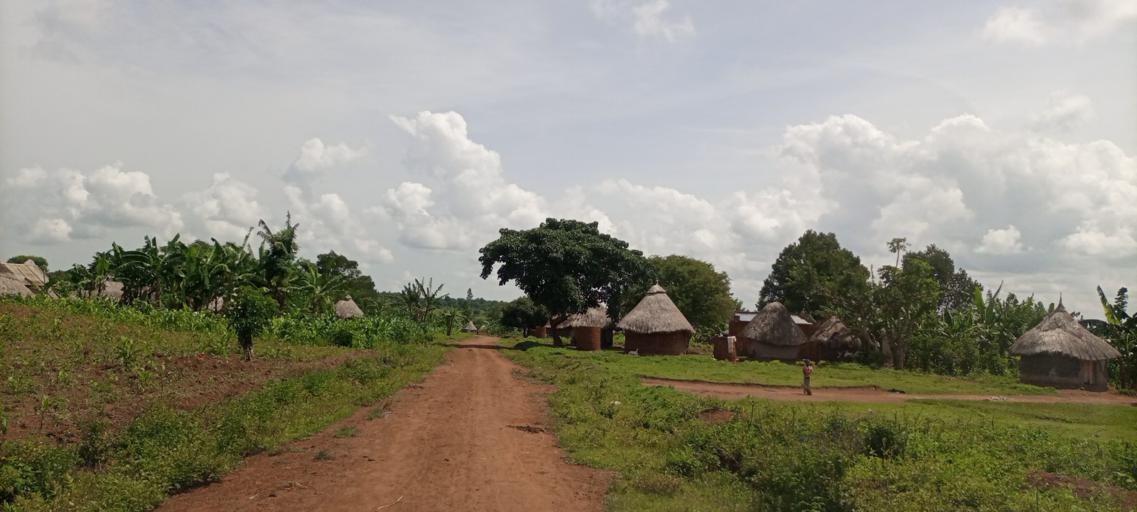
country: UG
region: Eastern Region
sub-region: Budaka District
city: Budaka
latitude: 1.1720
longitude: 33.9569
